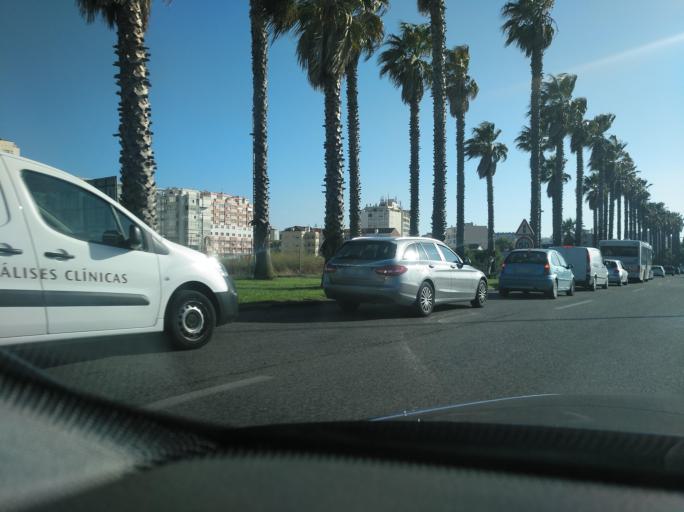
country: PT
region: Setubal
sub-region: Almada
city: Costa de Caparica
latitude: 38.6470
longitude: -9.2314
